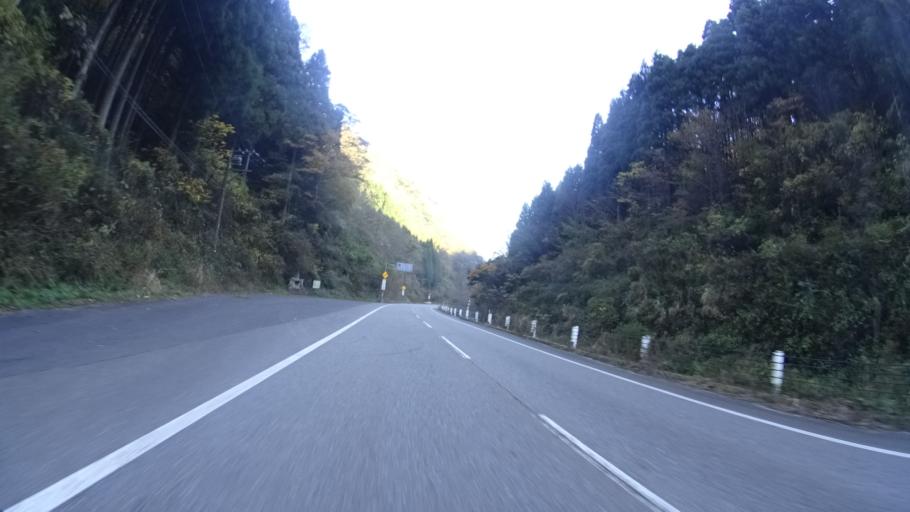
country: JP
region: Fukui
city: Maruoka
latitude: 36.1895
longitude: 136.3433
